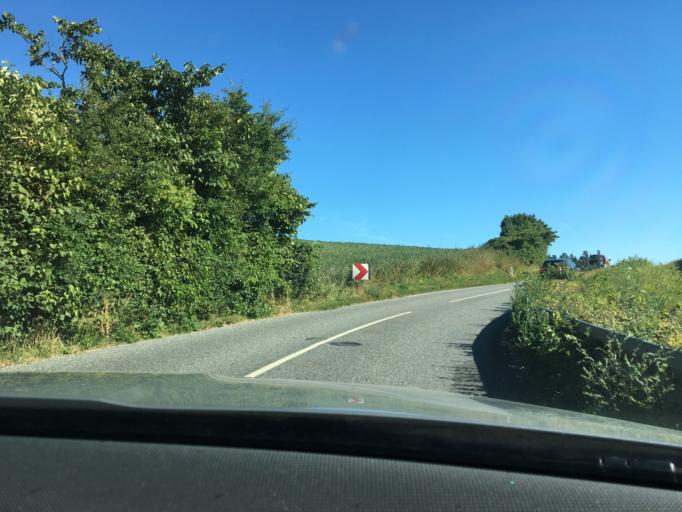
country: DK
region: Central Jutland
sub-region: Syddjurs Kommune
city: Hornslet
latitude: 56.3093
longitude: 10.3432
